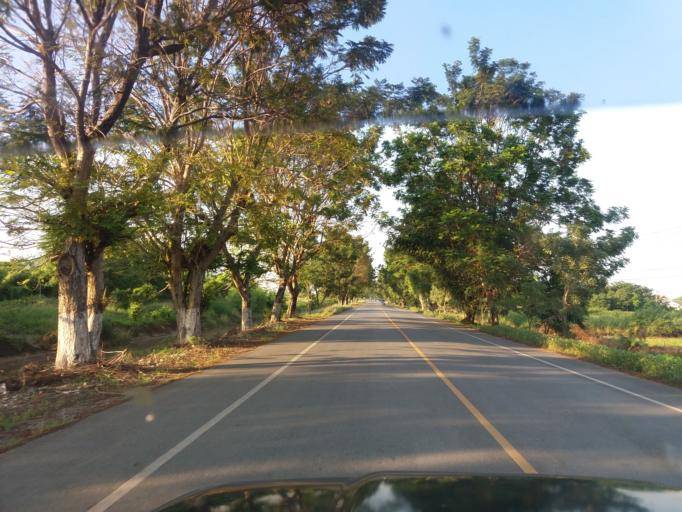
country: TH
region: Suphan Buri
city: Doem Bang Nang Buat
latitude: 14.8708
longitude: 100.0776
